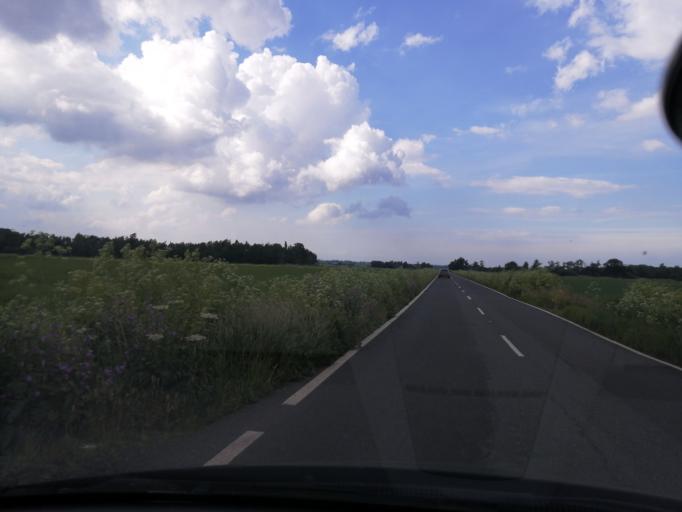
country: GB
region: England
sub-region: Cambridgeshire
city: Yaxley
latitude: 52.4846
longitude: -0.2430
